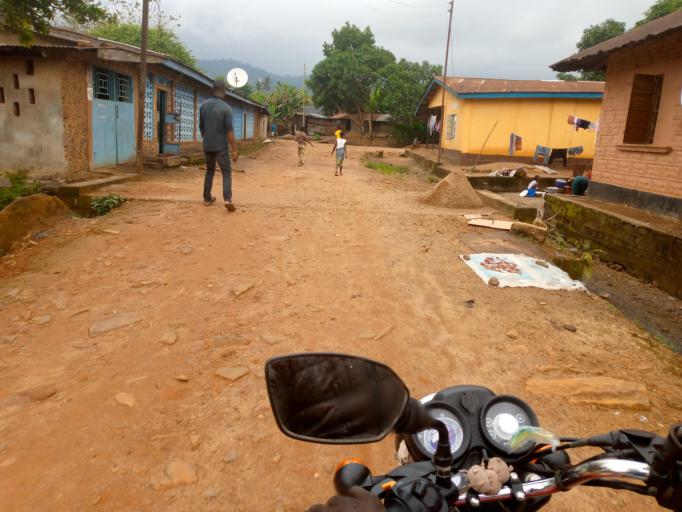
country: SL
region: Eastern Province
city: Kenema
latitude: 7.8784
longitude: -11.1859
